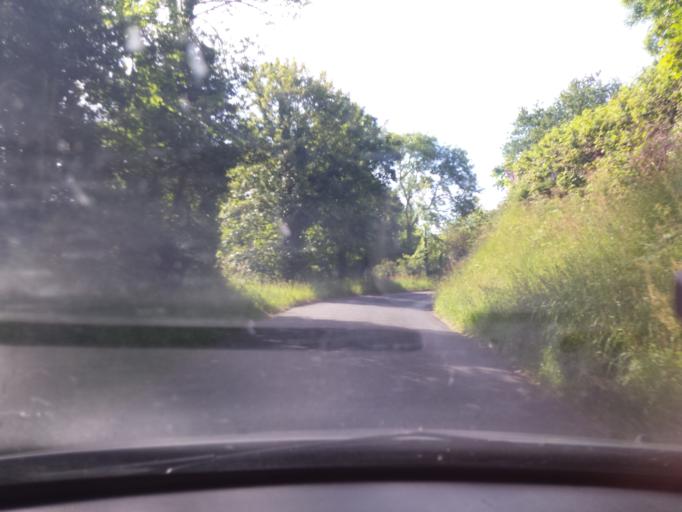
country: FR
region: Lower Normandy
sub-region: Departement de la Manche
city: Beaumont-Hague
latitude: 49.6844
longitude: -1.9229
